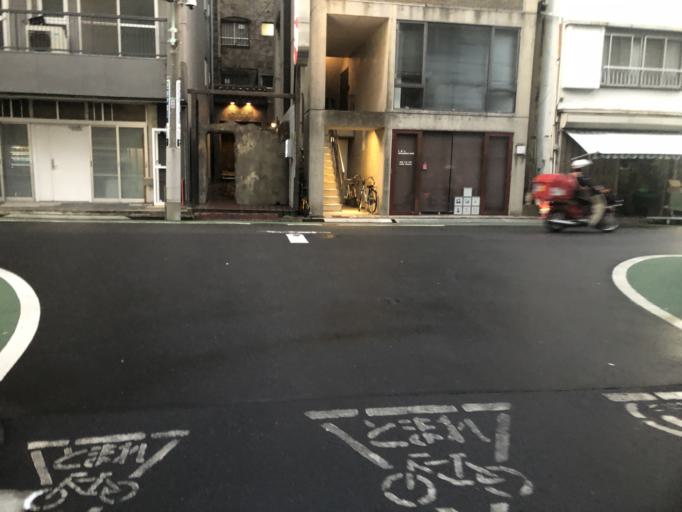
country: JP
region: Tokyo
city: Tokyo
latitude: 35.6576
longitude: 139.7403
